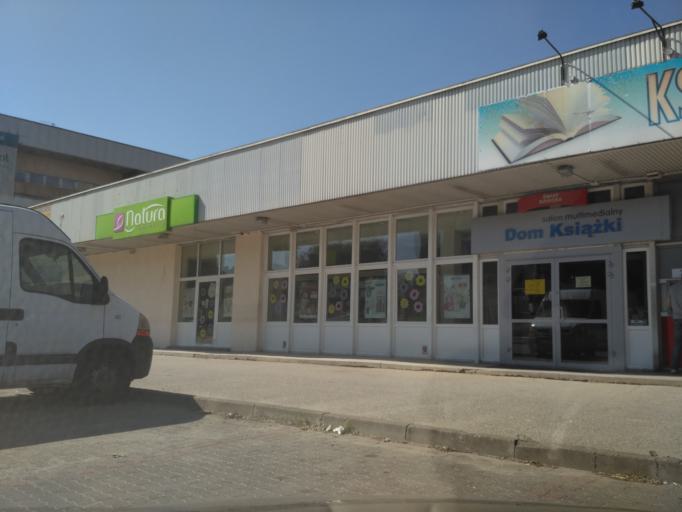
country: PL
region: Lublin Voivodeship
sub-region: Powiat lubelski
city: Lublin
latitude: 51.2629
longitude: 22.5460
